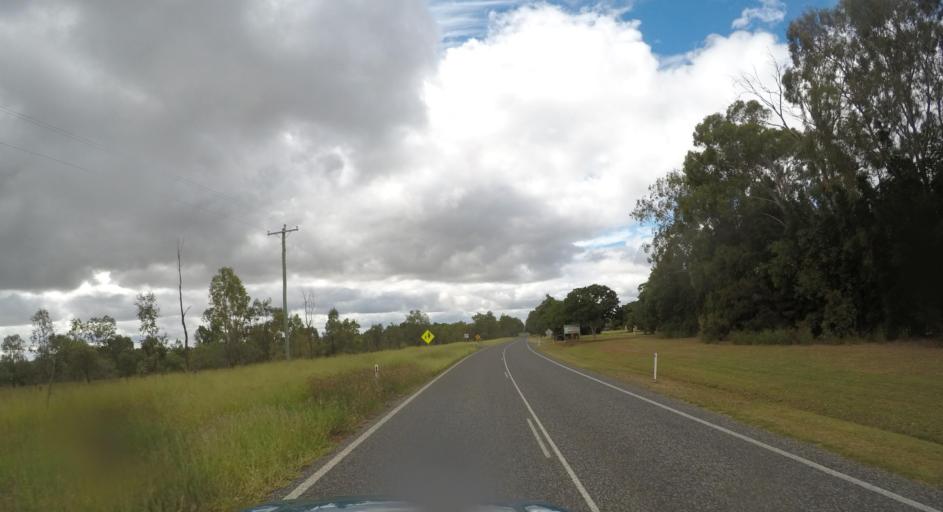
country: AU
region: Queensland
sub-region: North Burnett
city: Gayndah
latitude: -25.6305
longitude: 151.2813
